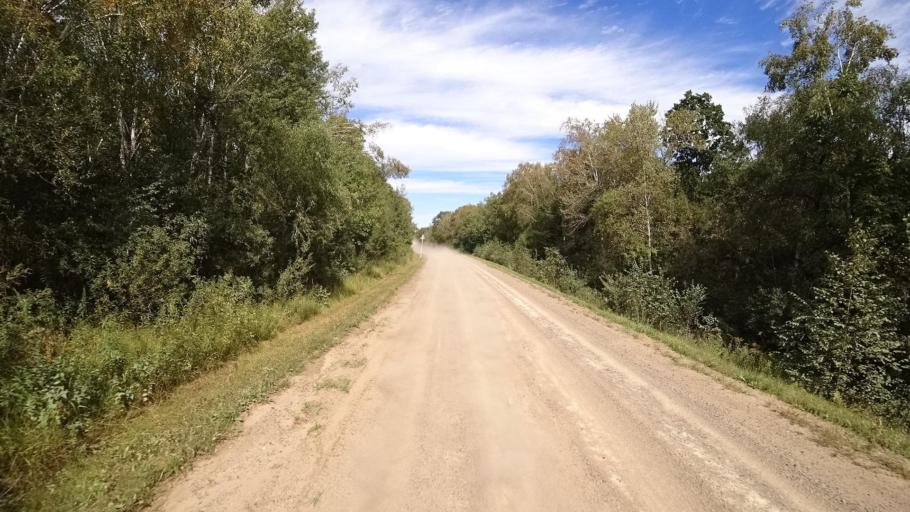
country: RU
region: Primorskiy
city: Yakovlevka
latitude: 44.6667
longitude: 133.6103
